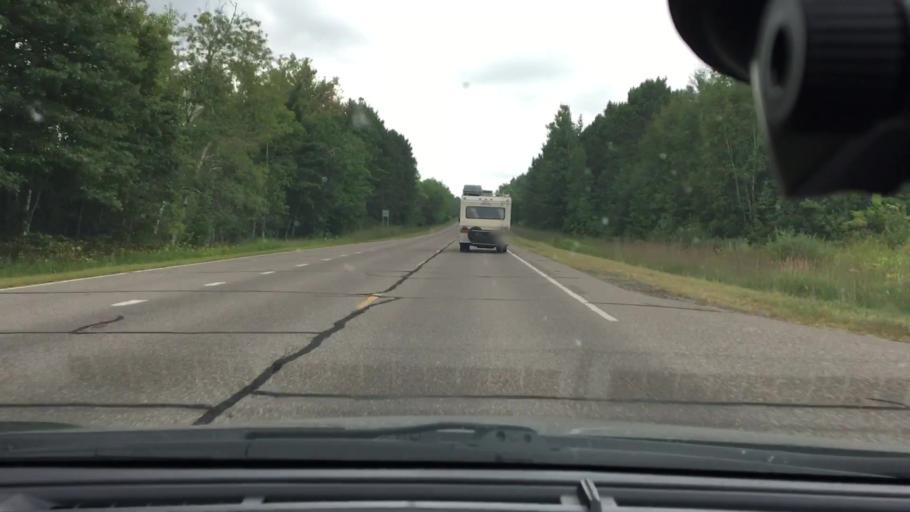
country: US
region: Minnesota
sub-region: Crow Wing County
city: Crosby
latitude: 46.4413
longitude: -93.8770
